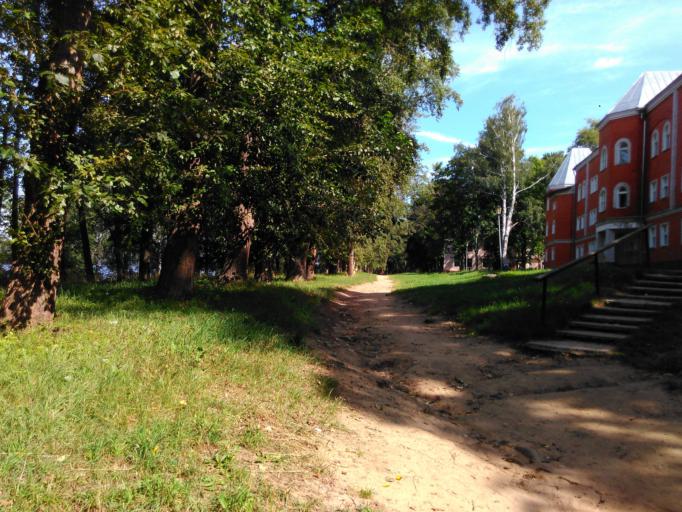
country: RU
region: Tverskaya
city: Konakovo
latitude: 56.6864
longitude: 36.6959
